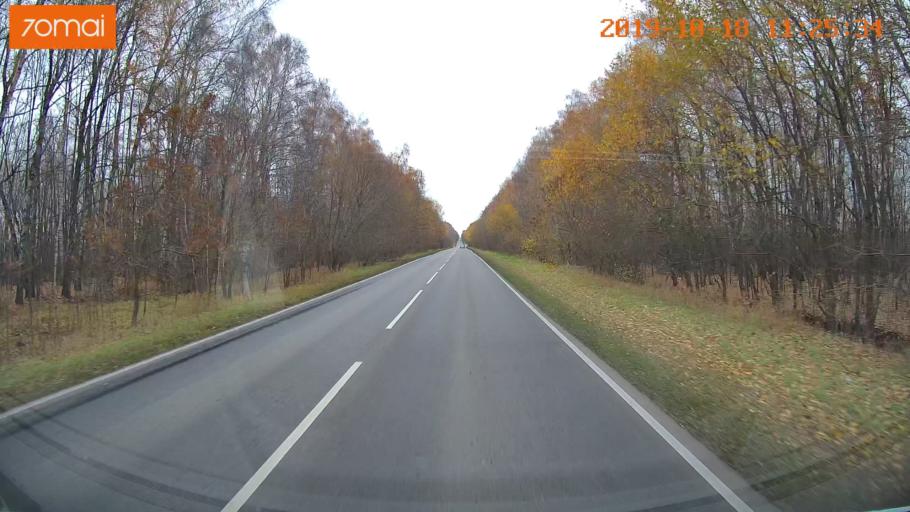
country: RU
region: Tula
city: Kimovsk
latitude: 54.1255
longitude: 38.6206
